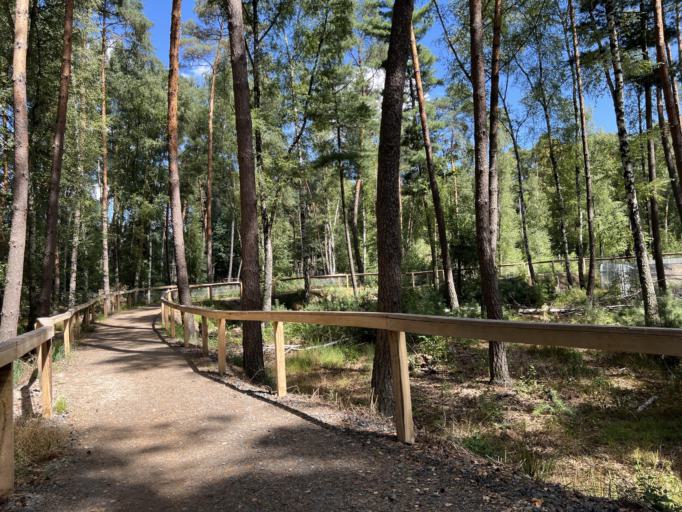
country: DE
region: Hesse
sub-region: Regierungsbezirk Darmstadt
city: Hanau am Main
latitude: 50.0832
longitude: 8.9028
